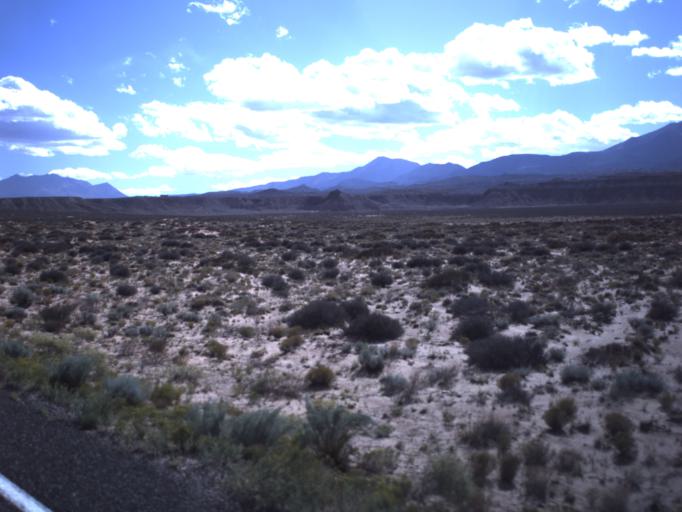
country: US
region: Utah
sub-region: Wayne County
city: Loa
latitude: 38.1694
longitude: -110.6238
